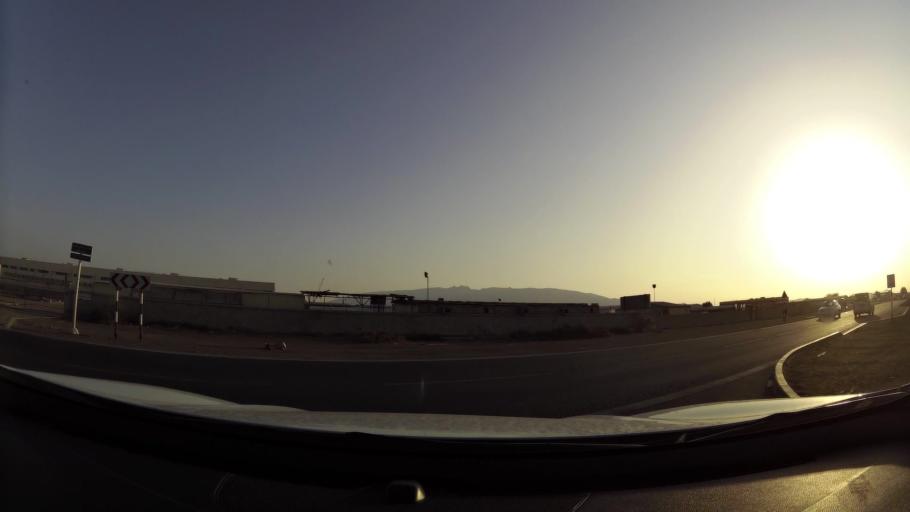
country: AE
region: Abu Dhabi
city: Al Ain
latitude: 24.1504
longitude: 55.8245
